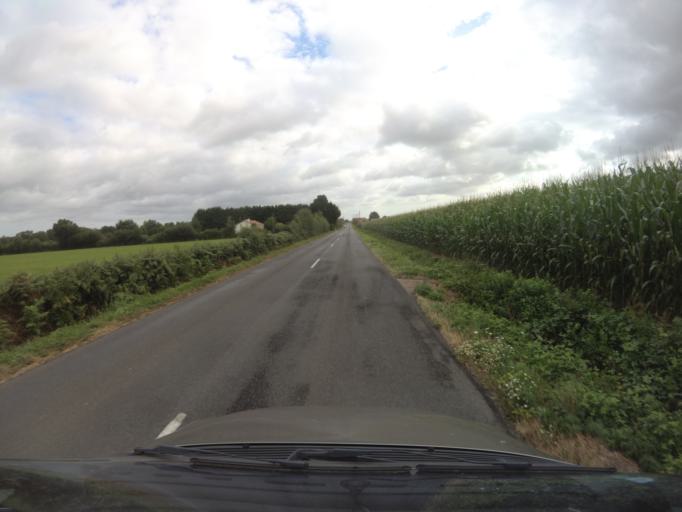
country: FR
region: Pays de la Loire
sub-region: Departement de Maine-et-Loire
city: Villedieu-la-Blouere
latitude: 47.1352
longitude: -1.0787
